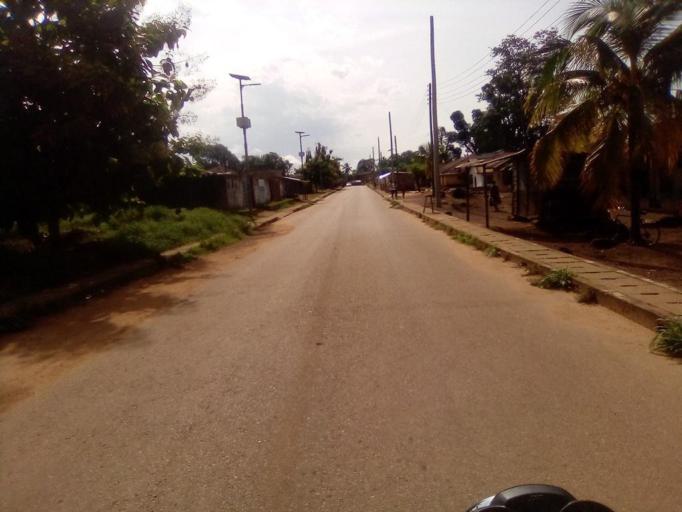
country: SL
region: Southern Province
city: Pujehun
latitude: 7.3571
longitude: -11.7181
